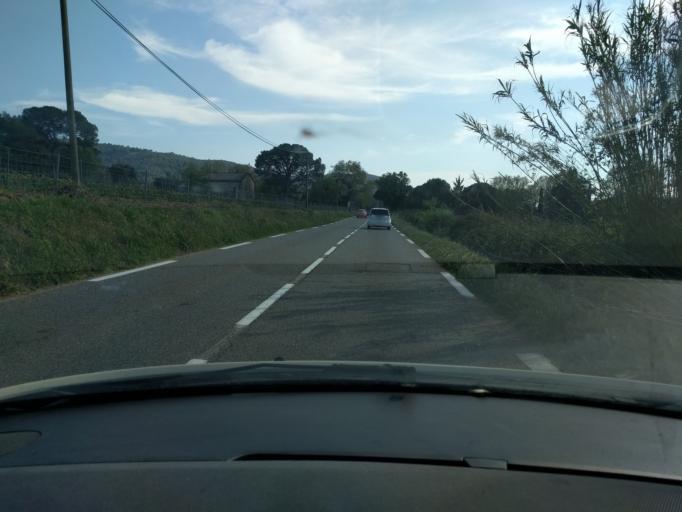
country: FR
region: Provence-Alpes-Cote d'Azur
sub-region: Departement du Var
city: Pierrefeu-du-Var
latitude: 43.2050
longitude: 6.1361
